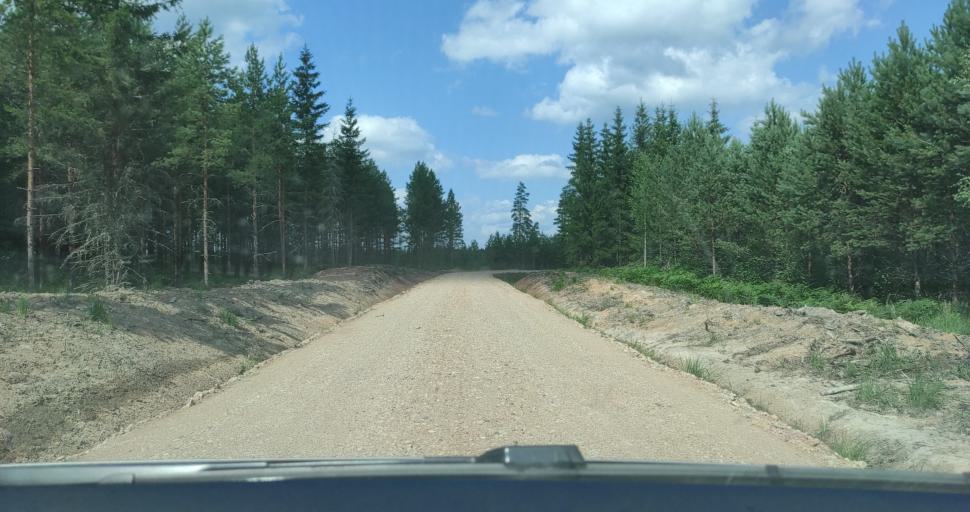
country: LV
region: Kuldigas Rajons
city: Kuldiga
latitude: 57.0585
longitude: 22.1893
